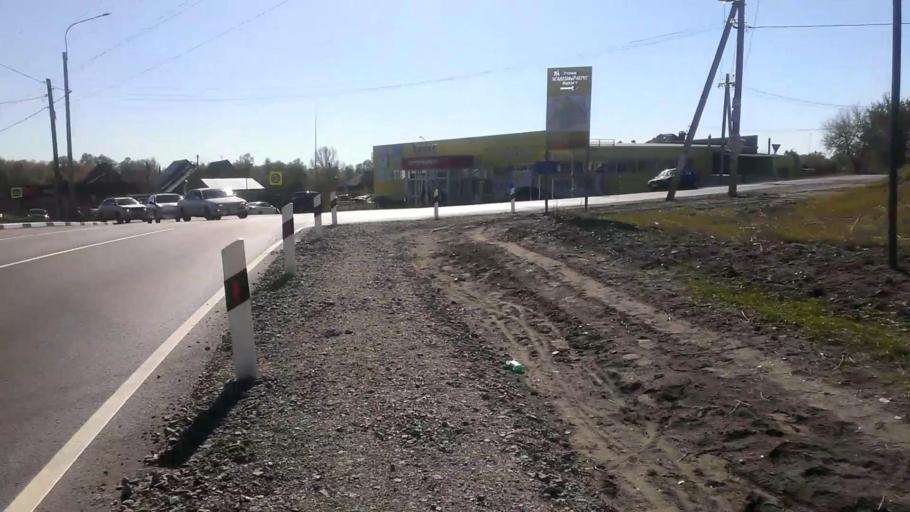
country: RU
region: Altai Krai
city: Sannikovo
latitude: 53.3189
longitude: 83.9444
